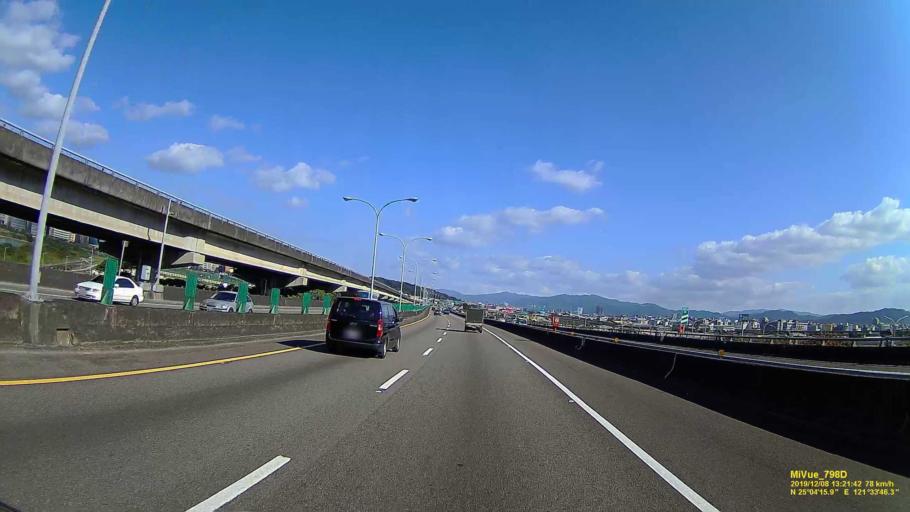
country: TW
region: Taipei
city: Taipei
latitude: 25.0716
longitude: 121.5637
